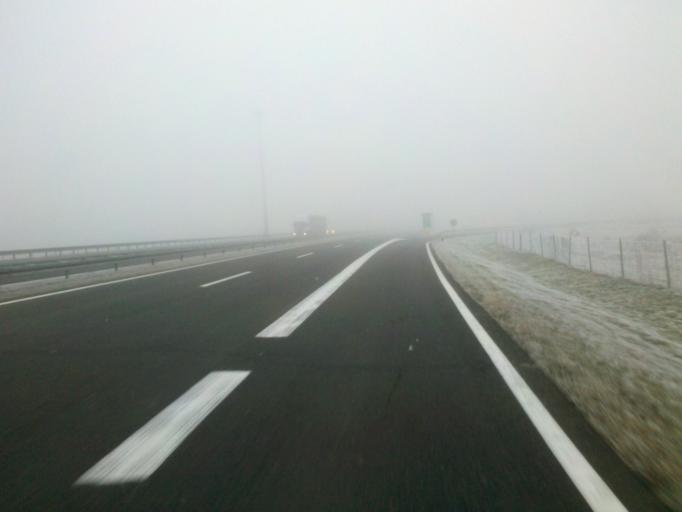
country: HR
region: Medimurska
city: Kursanec
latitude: 46.2576
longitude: 16.3991
